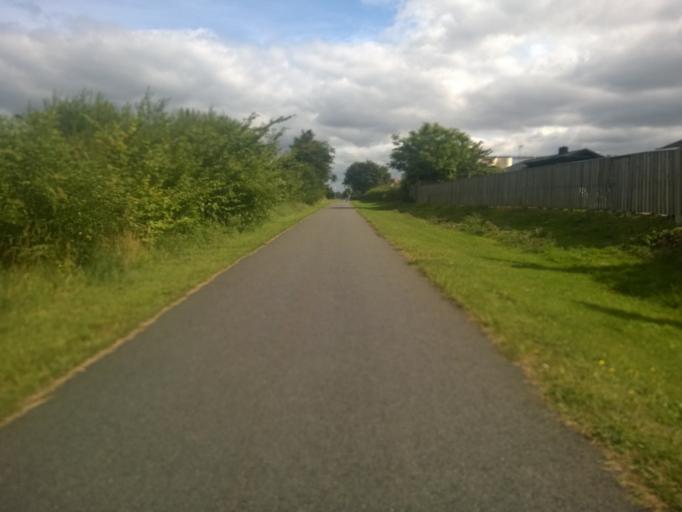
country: SE
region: Skane
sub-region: Kristianstads Kommun
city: Kristianstad
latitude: 56.0558
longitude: 14.1759
